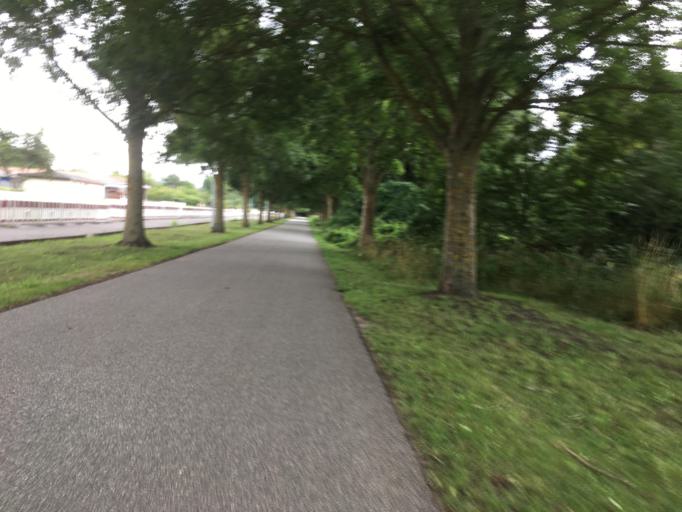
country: DE
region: Brandenburg
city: Prenzlau
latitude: 53.3000
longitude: 13.8651
